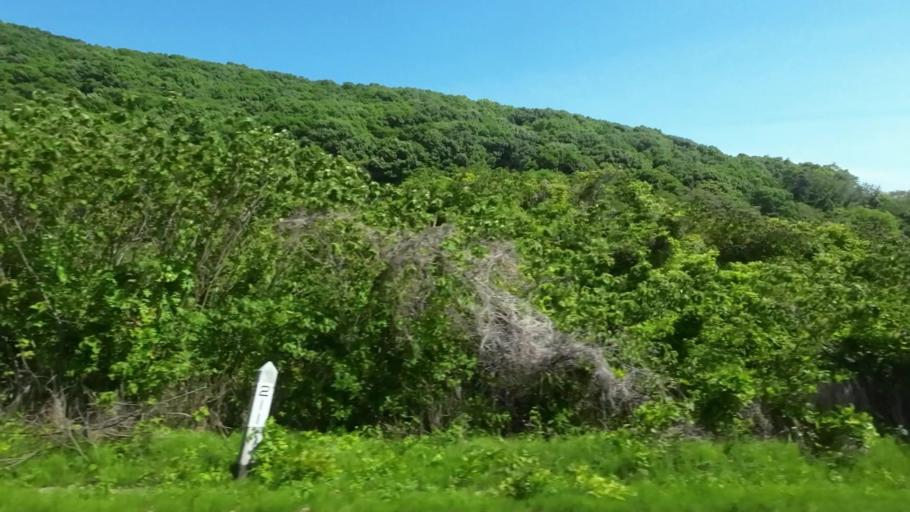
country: JP
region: Hiroshima
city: Onomichi
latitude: 34.4567
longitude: 133.2721
